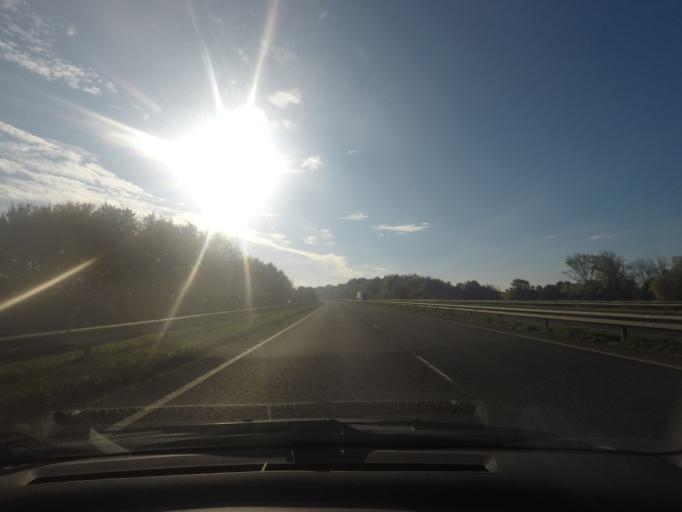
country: GB
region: England
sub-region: North Lincolnshire
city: Barton upon Humber
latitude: 53.6437
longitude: -0.4499
